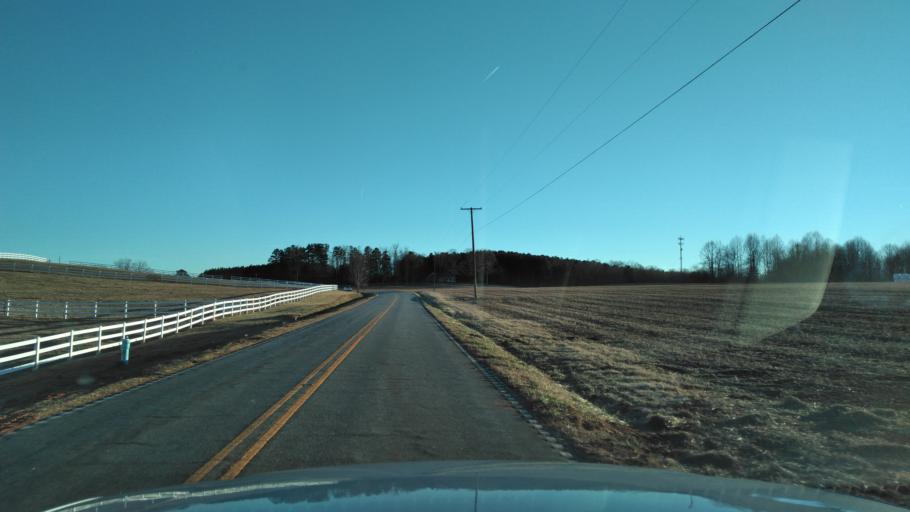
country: US
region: South Carolina
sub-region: Spartanburg County
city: Landrum
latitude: 35.2072
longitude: -82.0544
